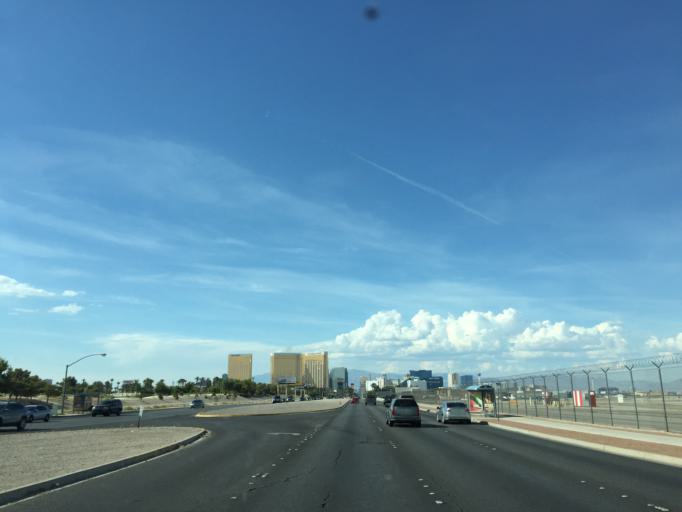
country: US
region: Nevada
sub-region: Clark County
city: Paradise
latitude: 36.0740
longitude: -115.1724
